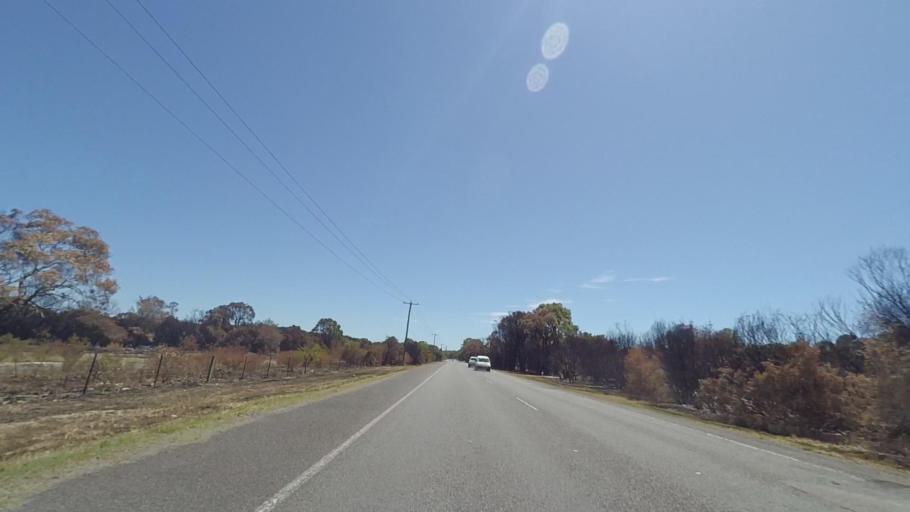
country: AU
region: New South Wales
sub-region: Port Stephens Shire
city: Medowie
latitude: -32.7873
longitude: 151.8558
